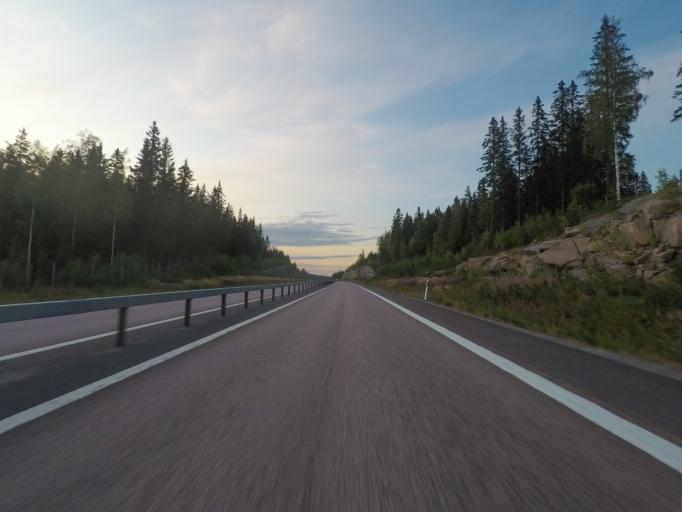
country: FI
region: Central Finland
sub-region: Jyvaeskylae
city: Saeynaetsalo
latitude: 62.1793
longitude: 25.9066
